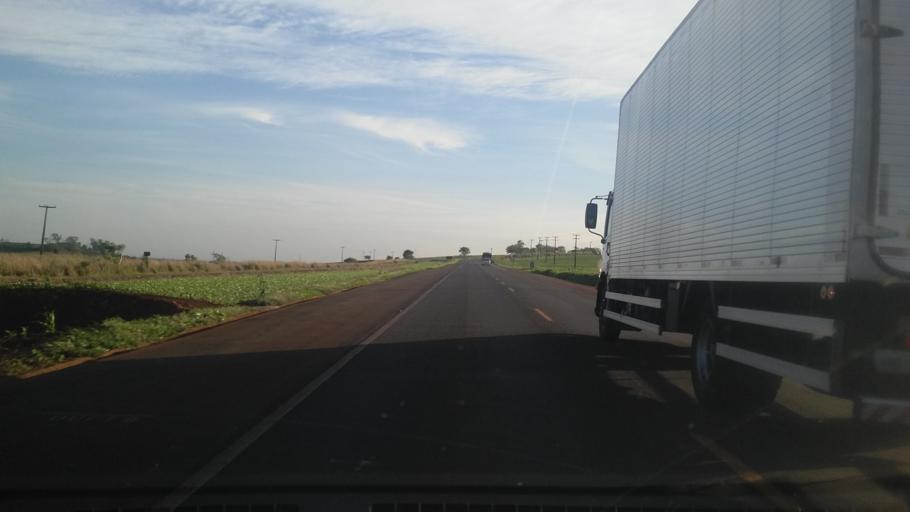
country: BR
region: Parana
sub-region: Bandeirantes
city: Bandeirantes
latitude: -23.1470
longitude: -50.5933
